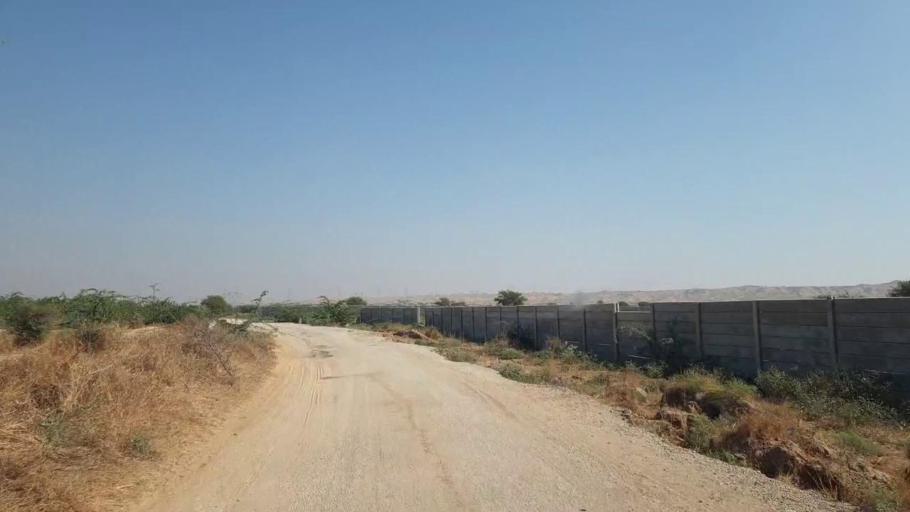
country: PK
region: Sindh
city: Gharo
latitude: 25.1834
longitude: 67.7366
